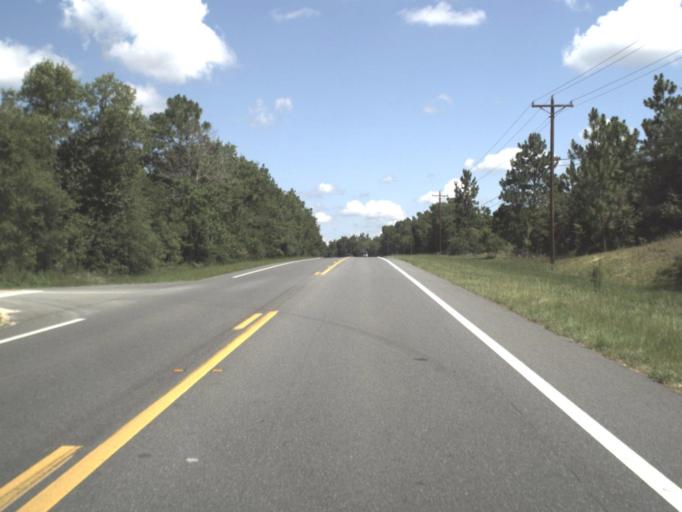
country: US
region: Florida
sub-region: Clay County
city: Keystone Heights
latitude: 29.7541
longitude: -81.9965
